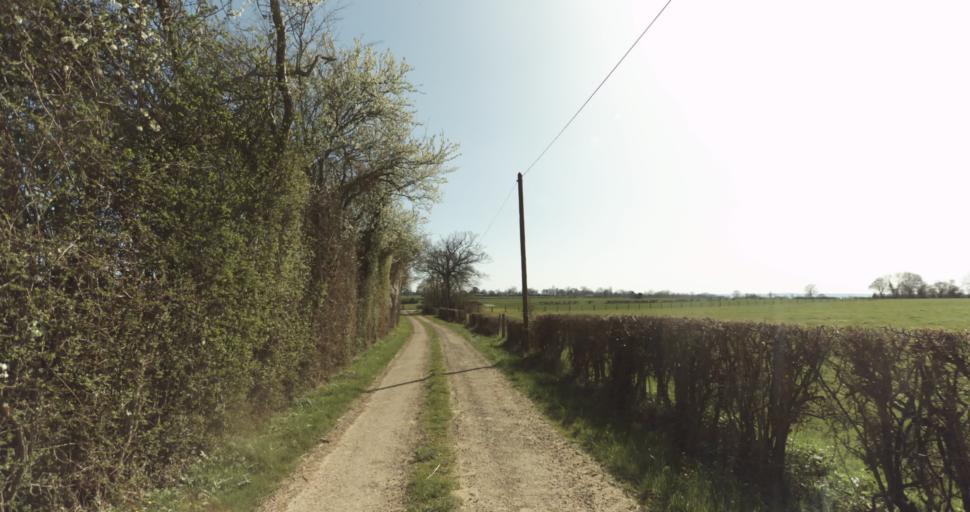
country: FR
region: Lower Normandy
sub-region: Departement du Calvados
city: Saint-Pierre-sur-Dives
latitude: 48.9375
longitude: -0.0061
